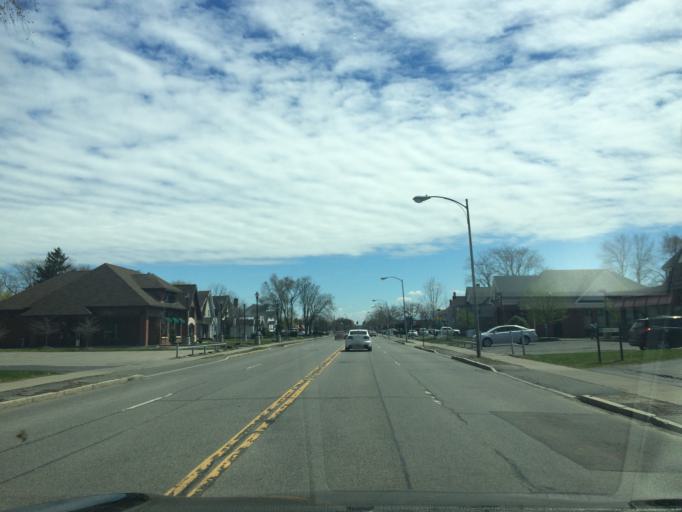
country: US
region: New York
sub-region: Monroe County
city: Brighton
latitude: 43.1314
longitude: -77.5701
